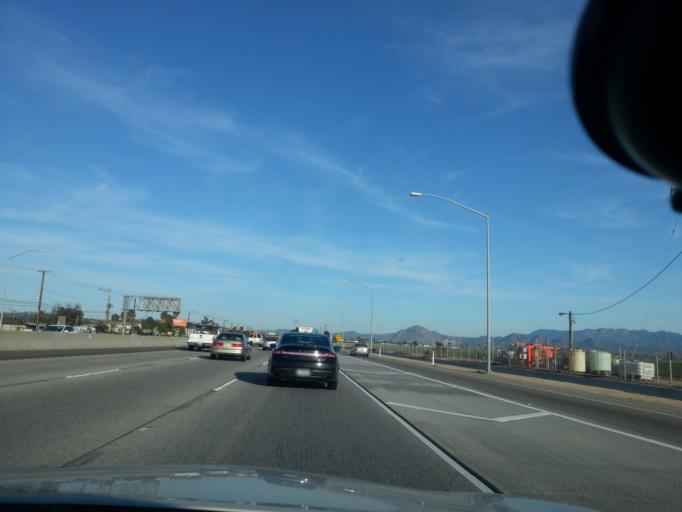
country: US
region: California
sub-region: Ventura County
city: El Rio
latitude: 34.2223
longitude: -119.1382
